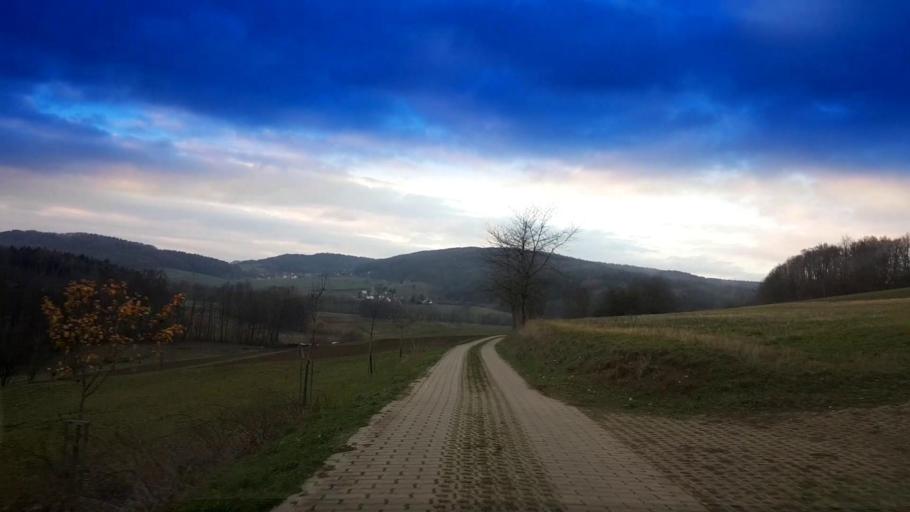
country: DE
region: Bavaria
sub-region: Upper Franconia
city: Schesslitz
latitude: 49.9991
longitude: 11.0759
